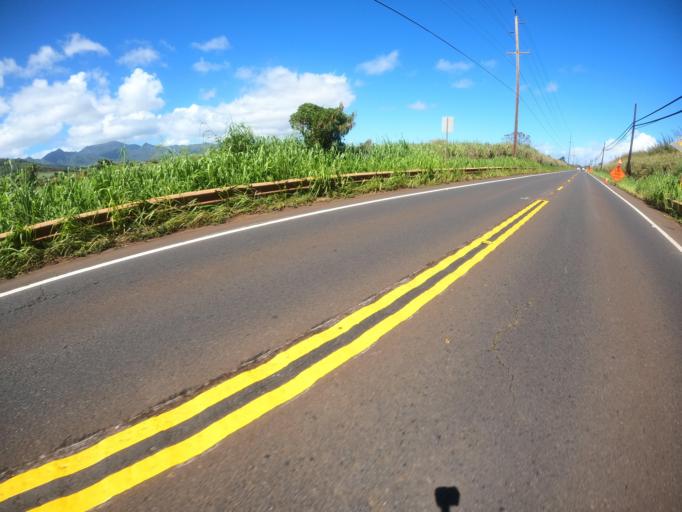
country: US
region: Hawaii
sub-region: Honolulu County
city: Schofield Barracks
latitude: 21.4671
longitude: -158.0543
